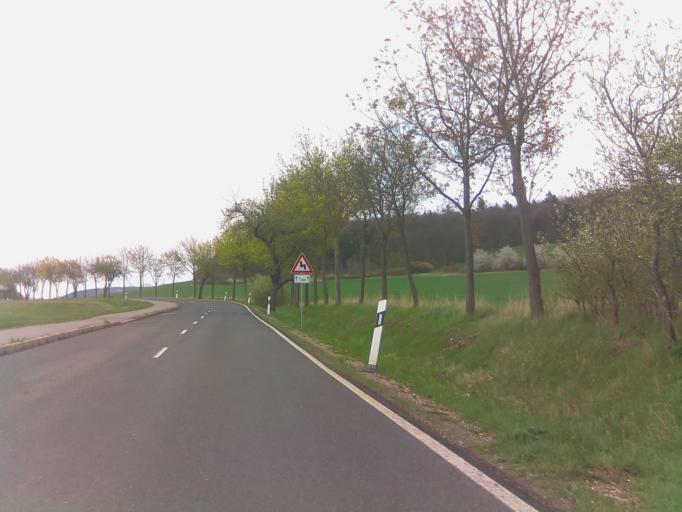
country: DE
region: Thuringia
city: Behringen
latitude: 50.7728
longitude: 11.0421
